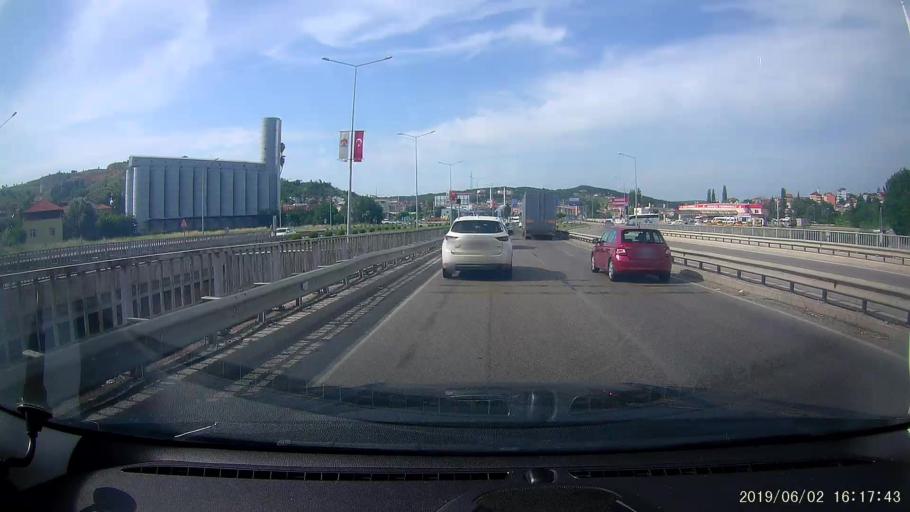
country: TR
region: Samsun
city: Havza
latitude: 40.9599
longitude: 35.6660
